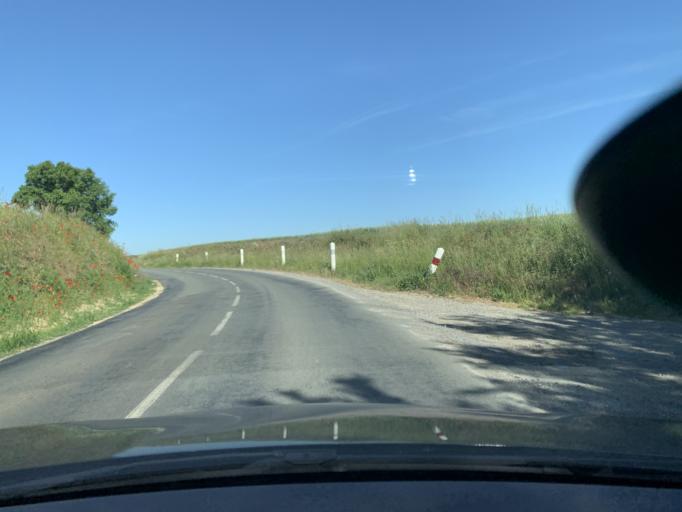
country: FR
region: Nord-Pas-de-Calais
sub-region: Departement du Nord
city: Fontaine-Notre-Dame
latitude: 50.1526
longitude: 3.1677
